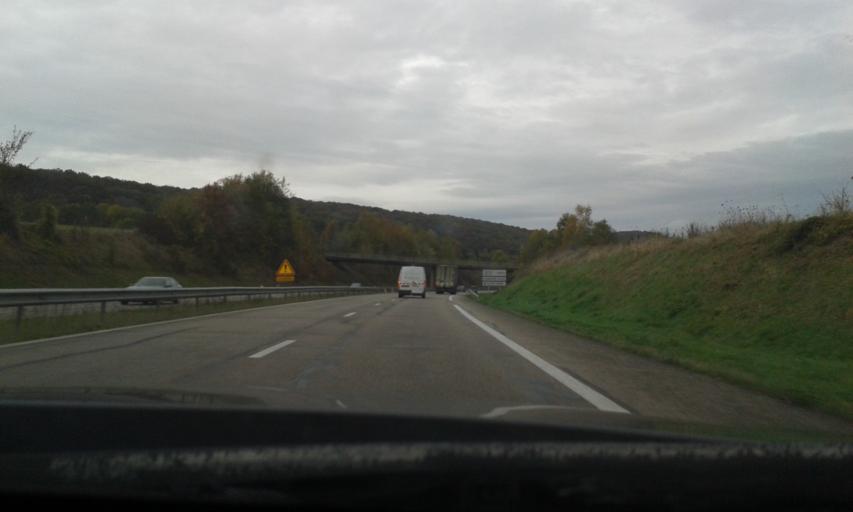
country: FR
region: Haute-Normandie
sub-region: Departement de l'Eure
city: Acquigny
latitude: 49.1690
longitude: 1.1720
